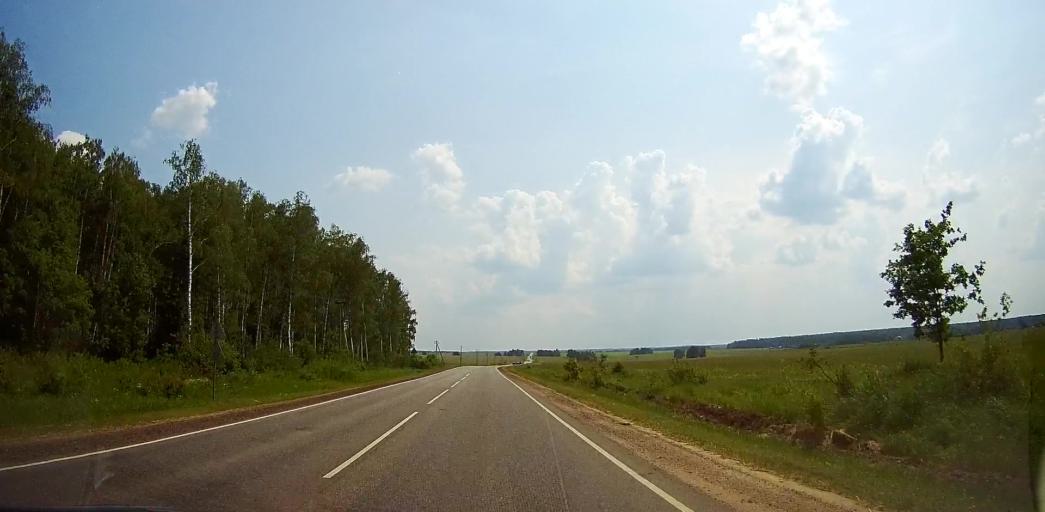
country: RU
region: Moskovskaya
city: Malino
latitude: 55.0537
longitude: 38.1432
